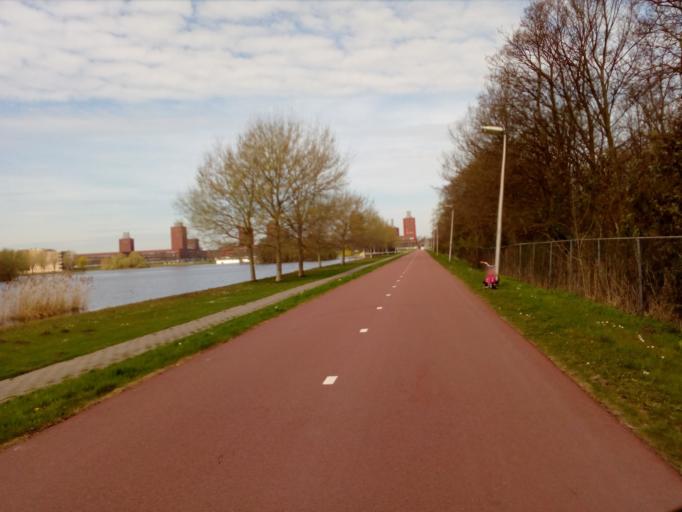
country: NL
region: South Holland
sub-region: Gemeente Den Haag
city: Ypenburg
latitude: 52.0380
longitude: 4.3770
